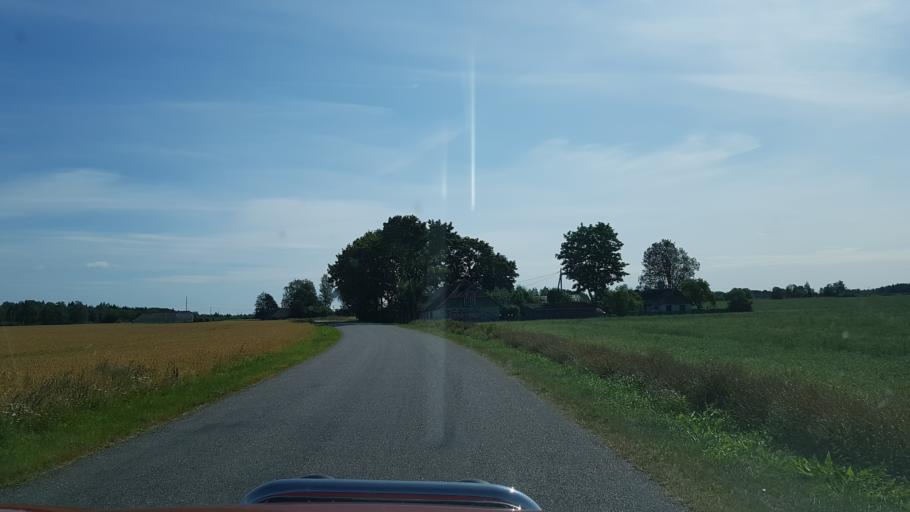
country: EE
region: Jaervamaa
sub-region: Jaerva-Jaani vald
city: Jarva-Jaani
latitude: 59.1145
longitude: 25.7436
